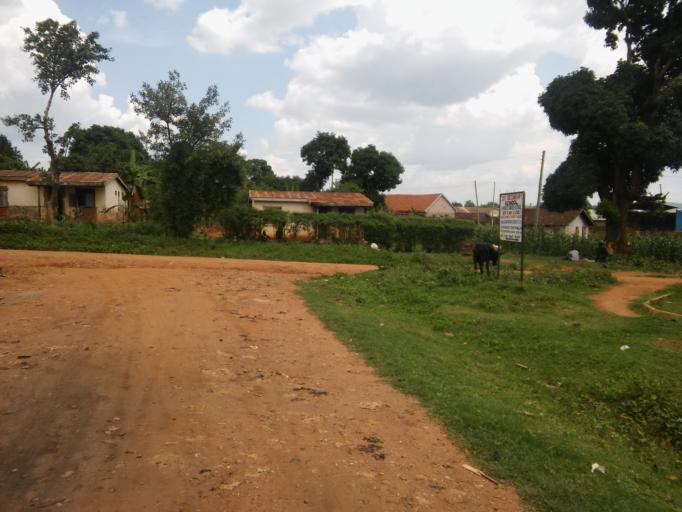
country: UG
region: Eastern Region
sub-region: Mbale District
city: Mbale
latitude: 1.0714
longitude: 34.1702
